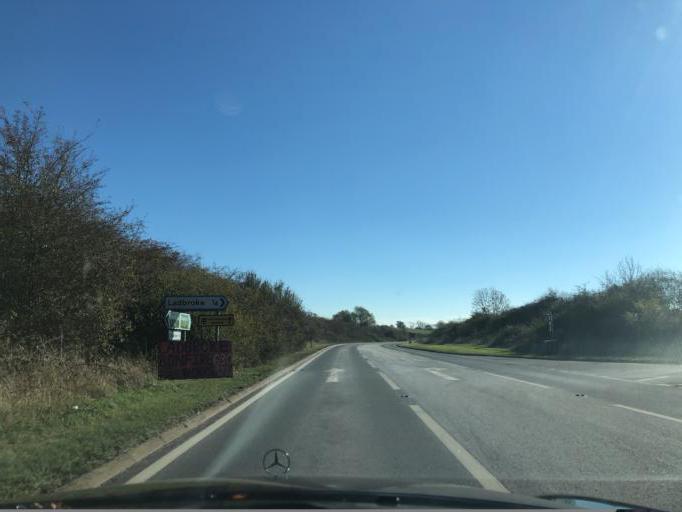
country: GB
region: England
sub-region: Warwickshire
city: Southam
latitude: 52.2314
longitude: -1.3895
